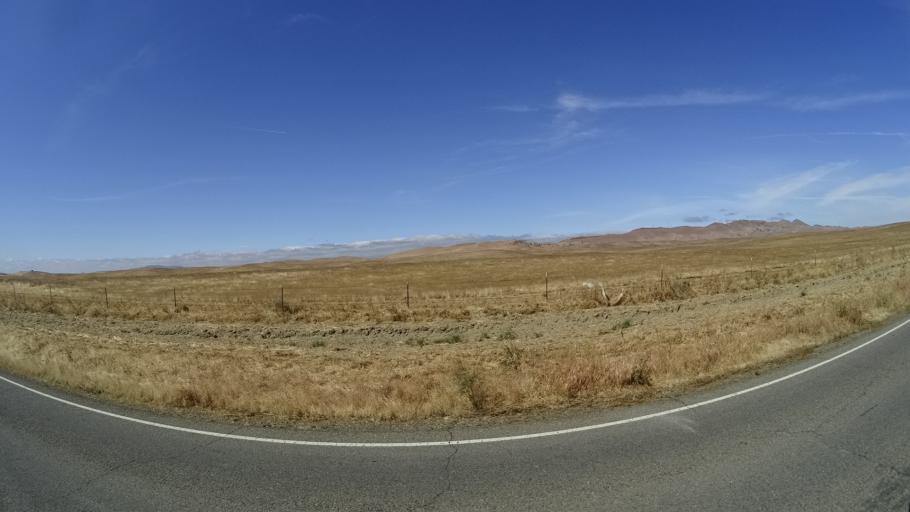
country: US
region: California
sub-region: Kings County
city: Avenal
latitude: 35.9146
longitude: -120.0675
